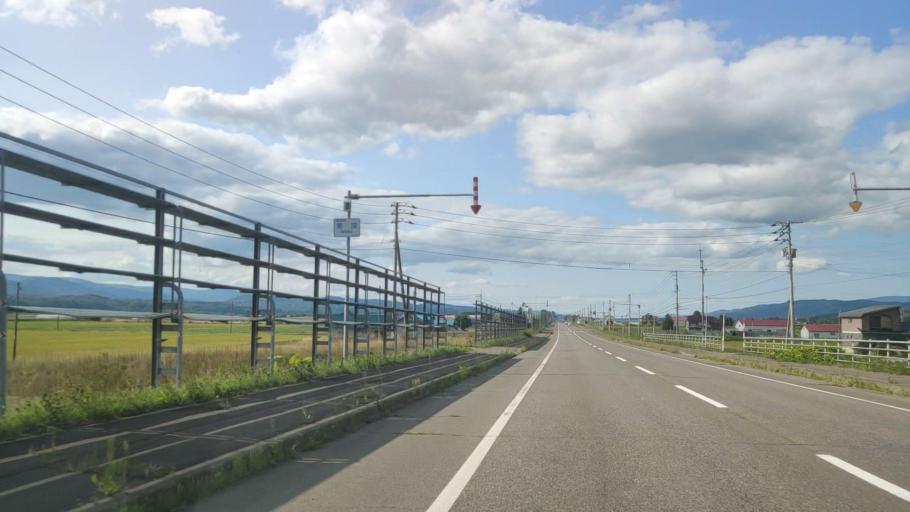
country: JP
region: Hokkaido
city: Nayoro
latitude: 44.4587
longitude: 142.3575
